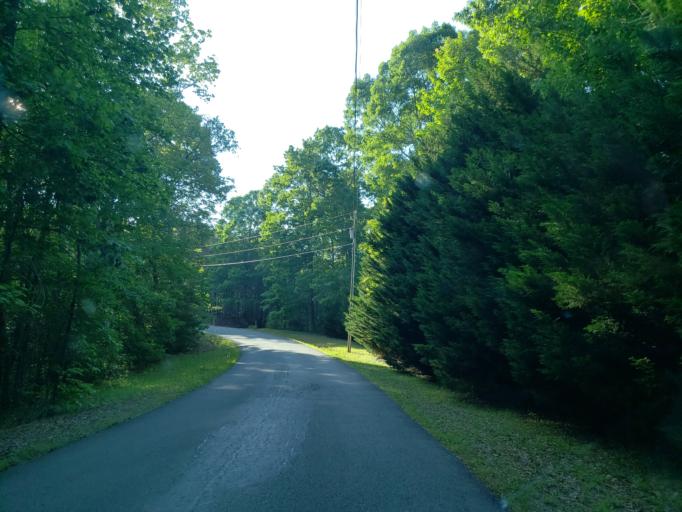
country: US
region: Georgia
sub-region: Gilmer County
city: Ellijay
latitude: 34.6588
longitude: -84.6426
